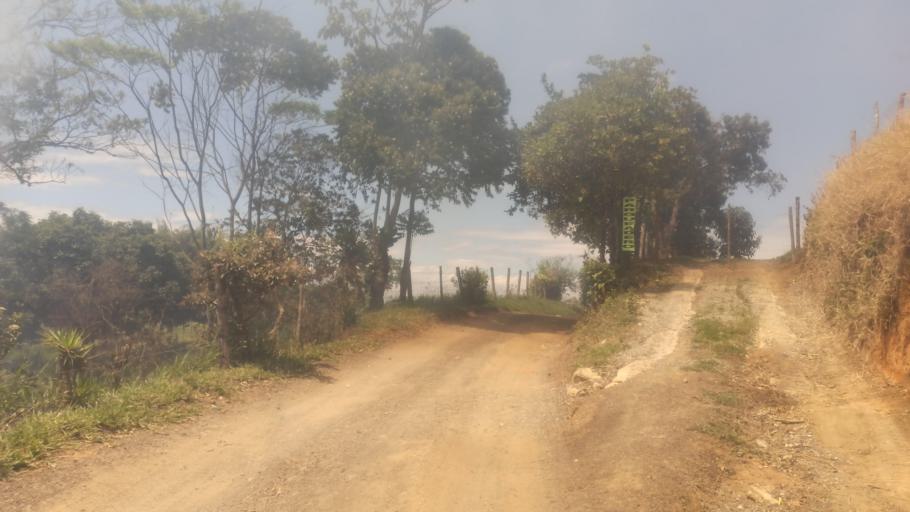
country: CO
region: Valle del Cauca
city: Jamundi
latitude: 3.1890
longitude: -76.6296
